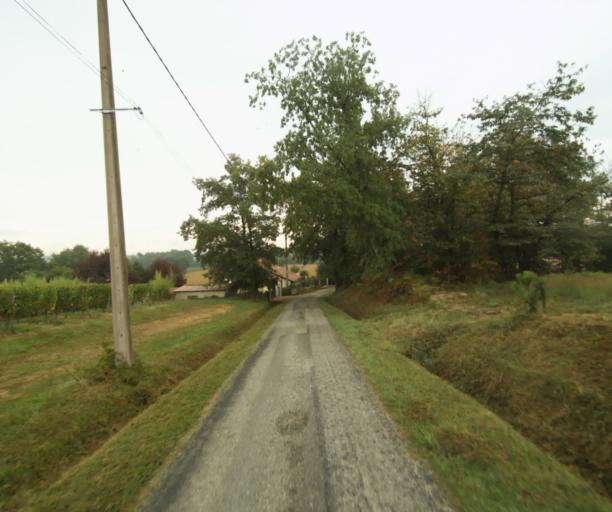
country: FR
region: Midi-Pyrenees
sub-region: Departement du Gers
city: Cazaubon
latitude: 43.9296
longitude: -0.1116
